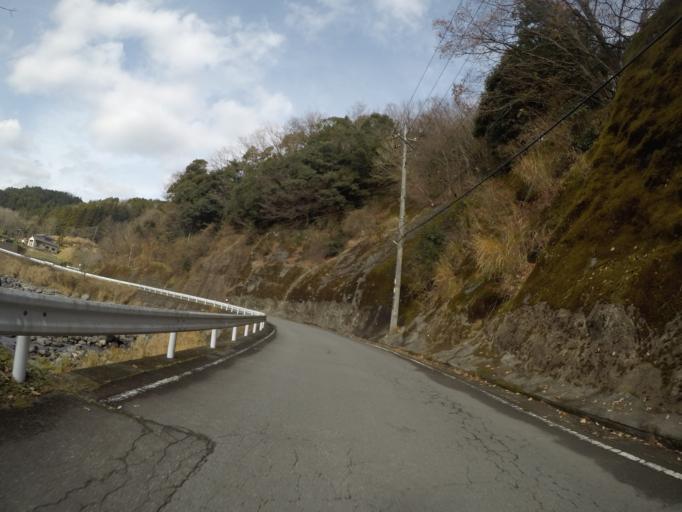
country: JP
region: Shizuoka
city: Heda
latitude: 34.8869
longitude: 138.9009
